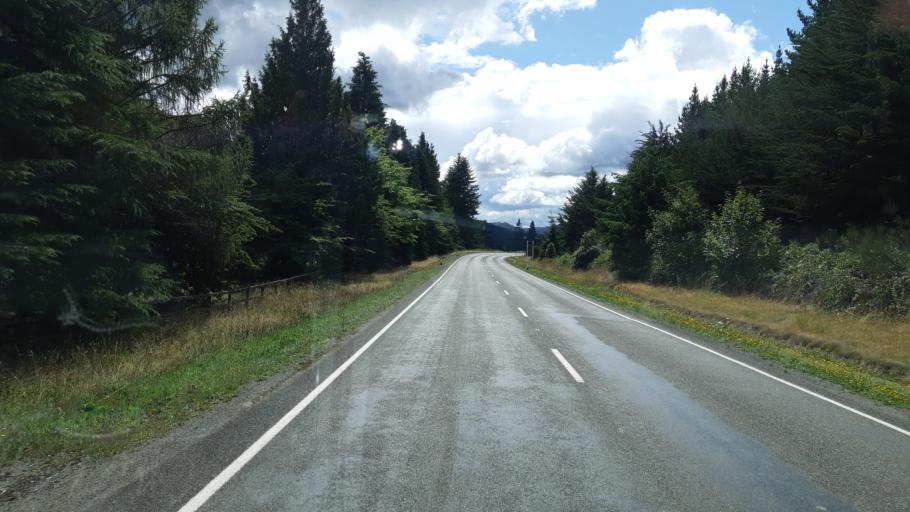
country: NZ
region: Tasman
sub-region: Tasman District
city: Wakefield
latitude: -41.5777
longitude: 172.7695
